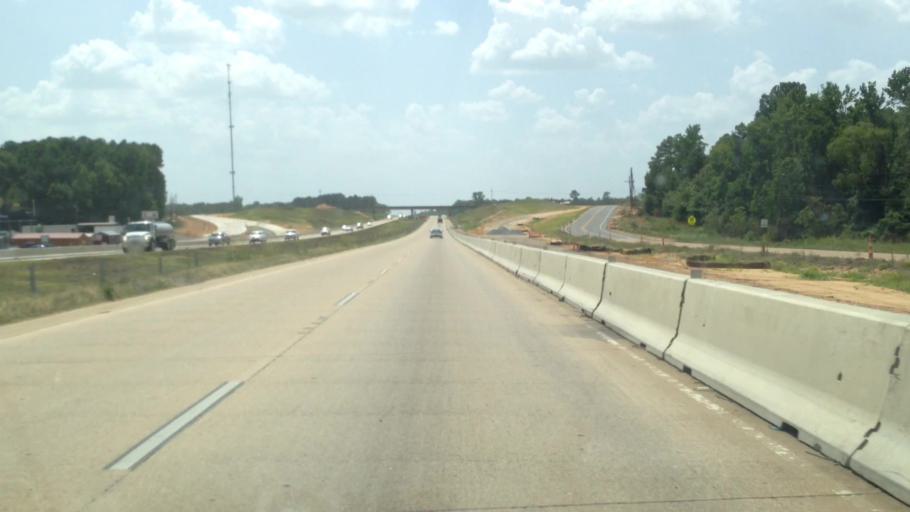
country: US
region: Louisiana
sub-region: Lincoln Parish
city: Ruston
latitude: 32.5405
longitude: -92.6714
